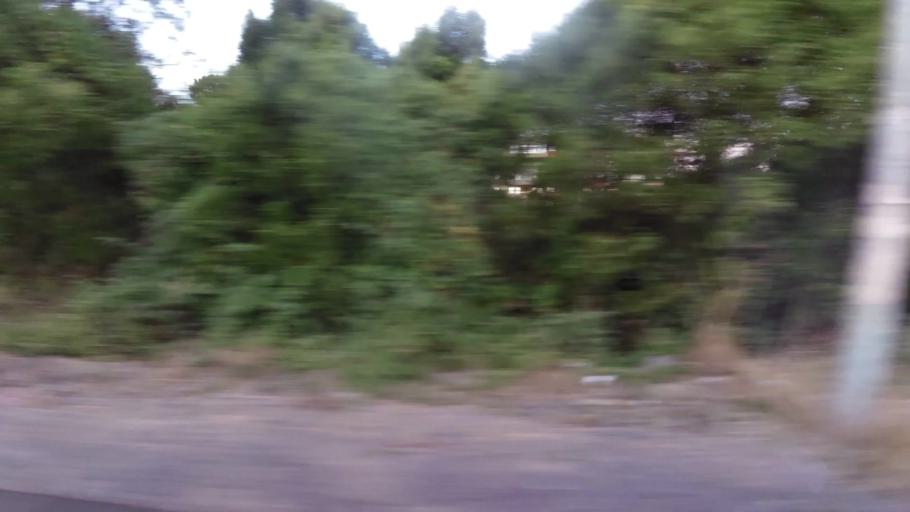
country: CL
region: Biobio
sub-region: Provincia de Concepcion
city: Concepcion
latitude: -36.8643
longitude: -73.0452
